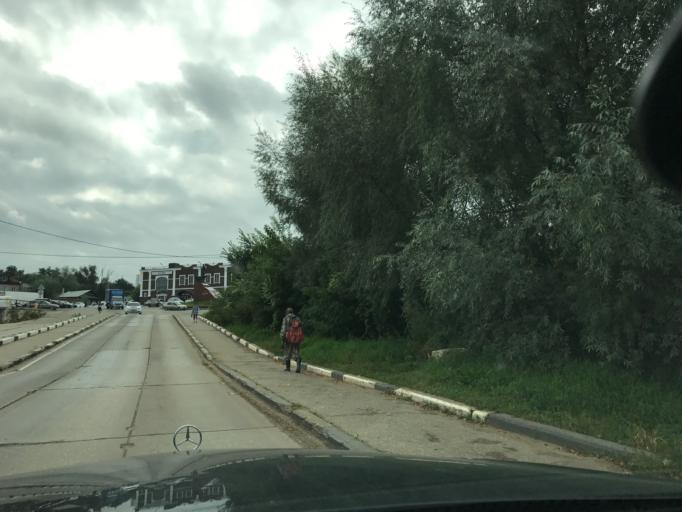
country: RU
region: Nizjnij Novgorod
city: Pavlovo
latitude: 55.9695
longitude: 43.0667
